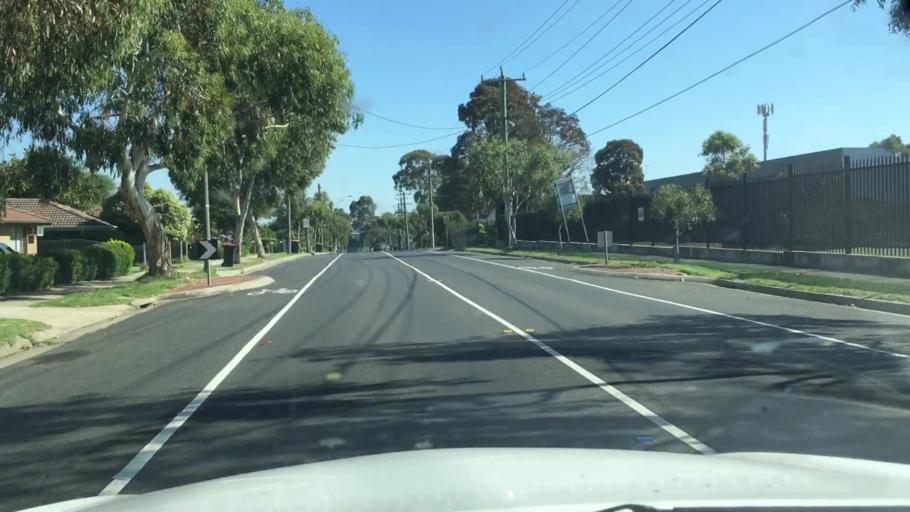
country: AU
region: Victoria
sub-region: Greater Dandenong
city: Noble Park North
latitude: -37.9466
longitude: 145.1878
